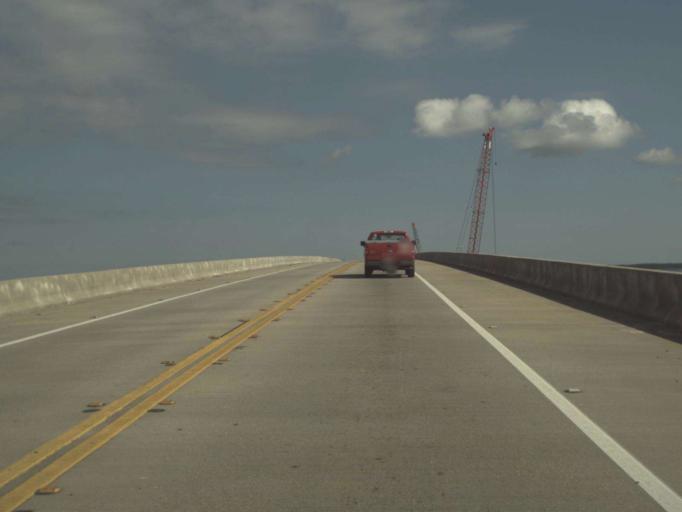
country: US
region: Florida
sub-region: Walton County
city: Seaside
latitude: 30.3984
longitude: -86.1696
